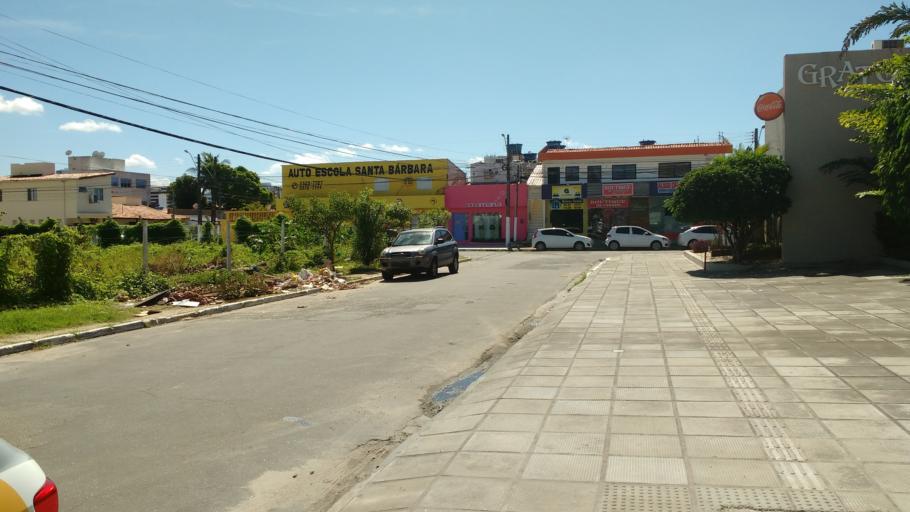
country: BR
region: Alagoas
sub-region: Maceio
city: Maceio
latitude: -9.6530
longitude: -35.7039
